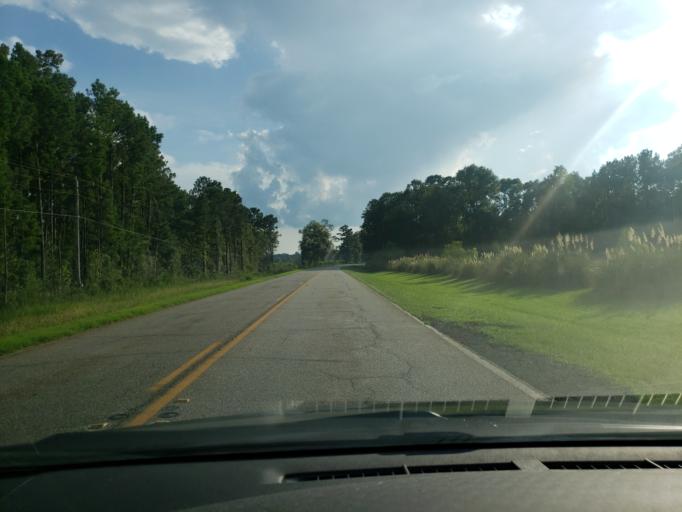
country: US
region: Georgia
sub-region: Dougherty County
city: Albany
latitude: 31.5760
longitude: -84.3056
